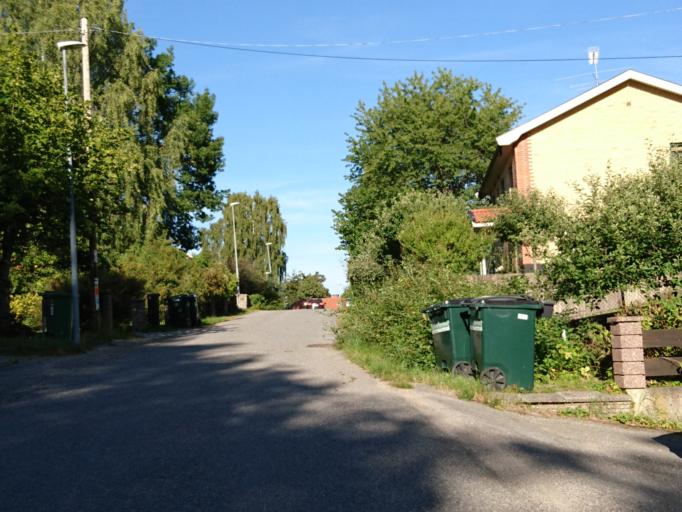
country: SE
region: Stockholm
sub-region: Huddinge Kommun
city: Segeltorp
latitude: 59.2692
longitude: 17.9472
